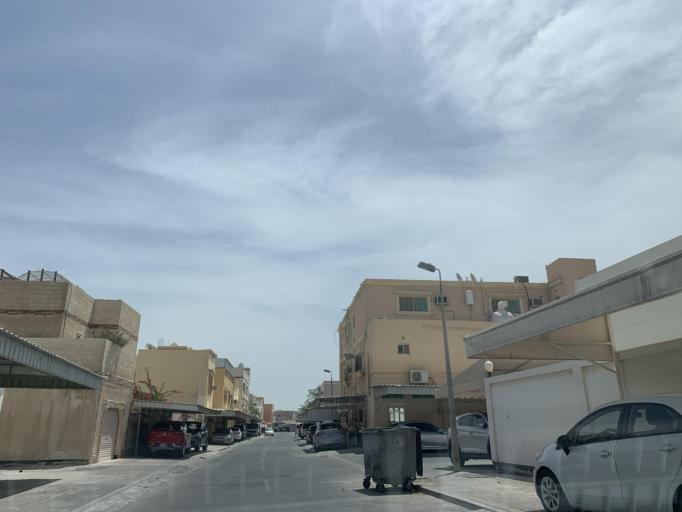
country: BH
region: Northern
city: Ar Rifa'
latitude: 26.1408
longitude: 50.5617
